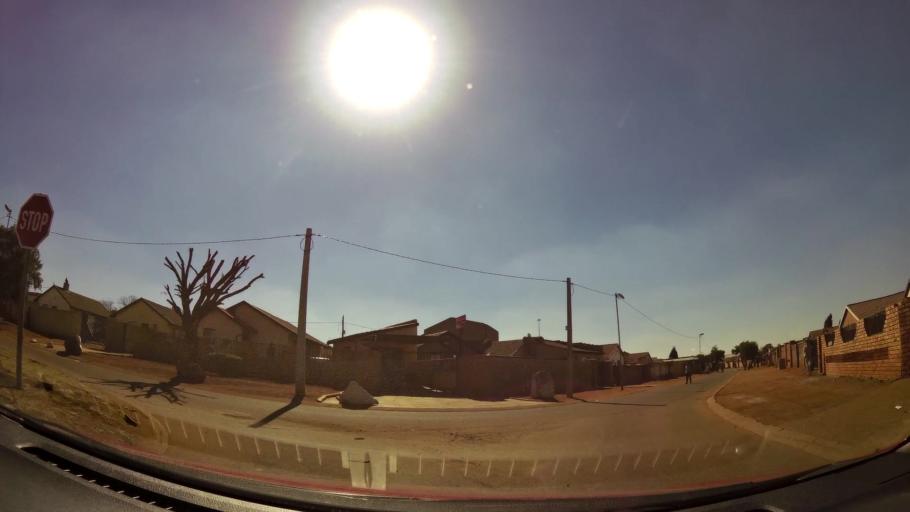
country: ZA
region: Gauteng
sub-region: City of Johannesburg Metropolitan Municipality
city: Soweto
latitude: -26.2485
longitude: 27.8060
